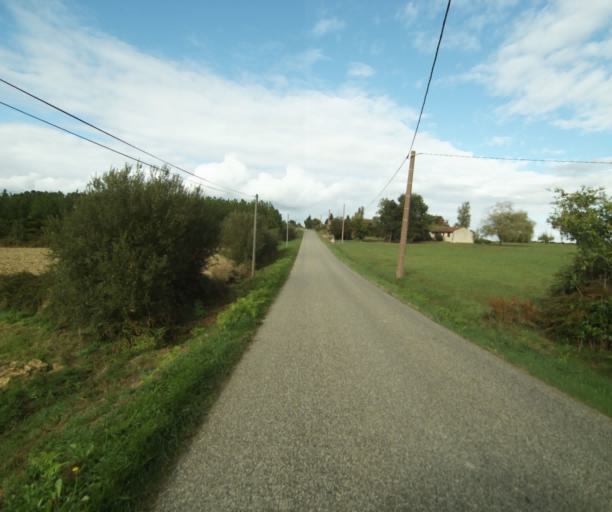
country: FR
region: Midi-Pyrenees
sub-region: Departement du Gers
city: Eauze
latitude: 43.9049
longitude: 0.1009
